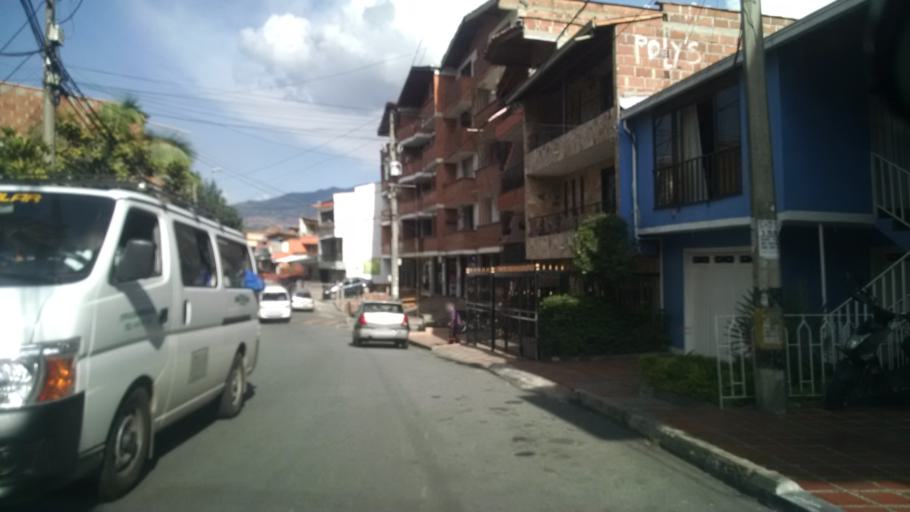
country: CO
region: Antioquia
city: Medellin
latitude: 6.2846
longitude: -75.5861
